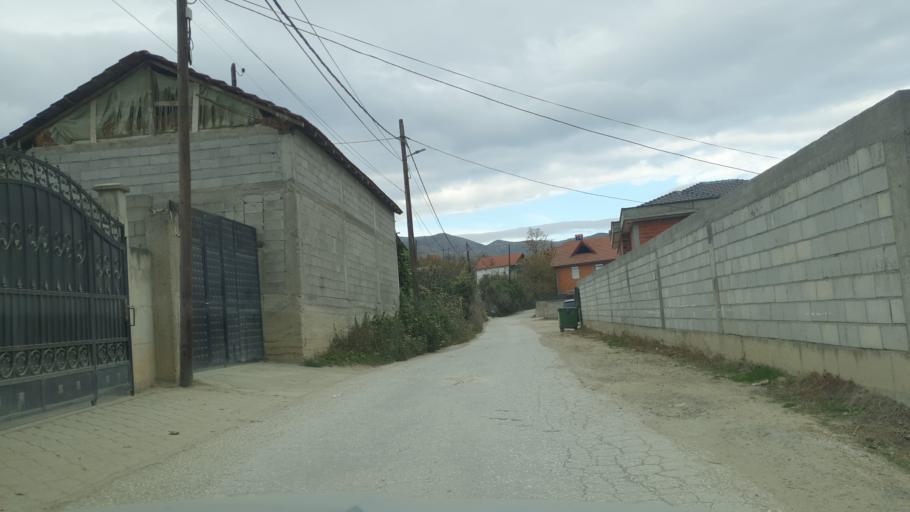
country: MK
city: Kondovo
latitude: 42.0330
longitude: 21.2832
